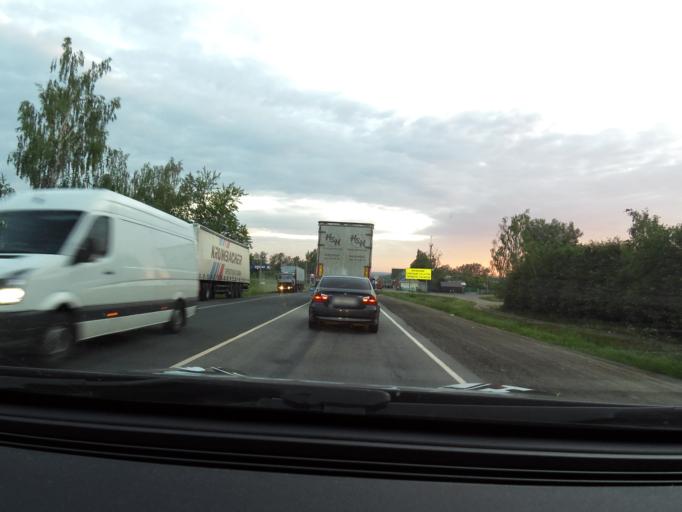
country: RU
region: Chuvashia
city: Yadrin
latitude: 56.0395
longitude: 46.2774
